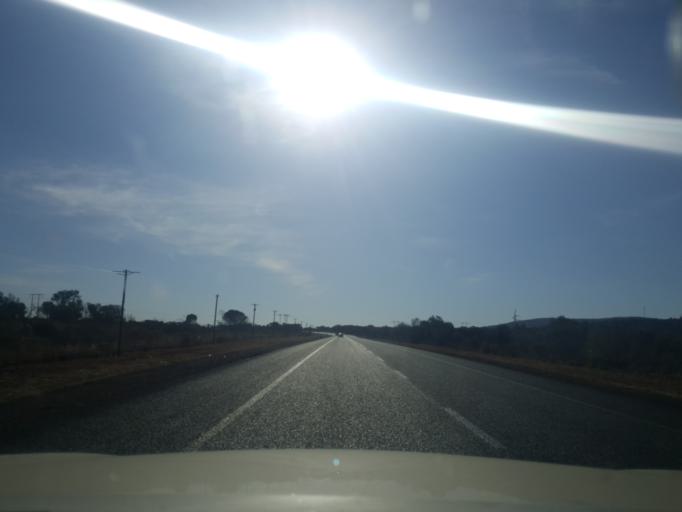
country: ZA
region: North-West
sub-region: Ngaka Modiri Molema District Municipality
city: Zeerust
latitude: -25.5429
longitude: 26.0457
